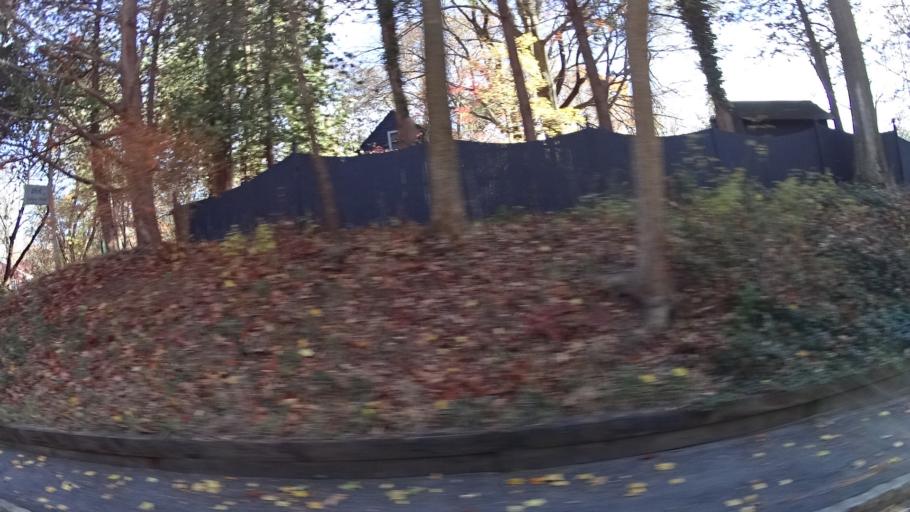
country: US
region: New Jersey
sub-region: Somerset County
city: Watchung
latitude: 40.6420
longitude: -74.4461
